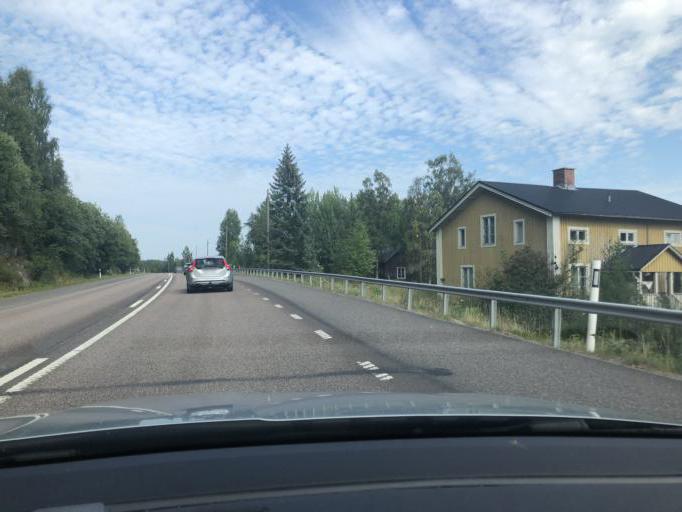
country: SE
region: Vaesternorrland
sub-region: Kramfors Kommun
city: Kramfors
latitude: 62.8867
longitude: 17.8523
